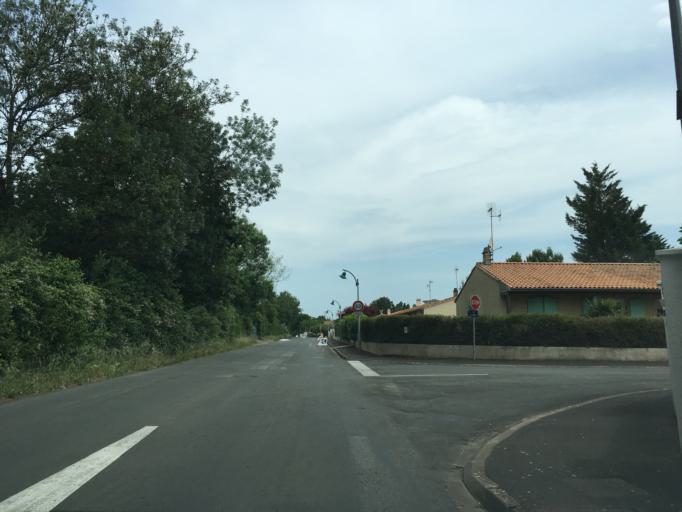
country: FR
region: Poitou-Charentes
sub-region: Departement des Deux-Sevres
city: Bessines
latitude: 46.3175
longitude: -0.5033
